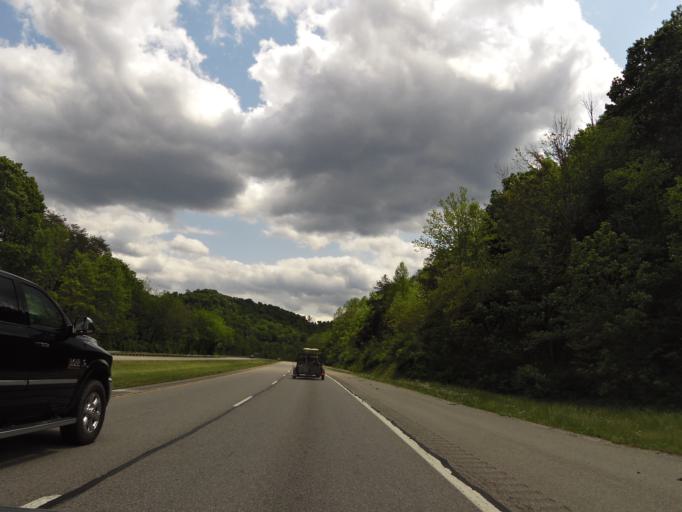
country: US
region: West Virginia
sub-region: Kanawha County
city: Sissonville
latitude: 38.5588
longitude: -81.6359
